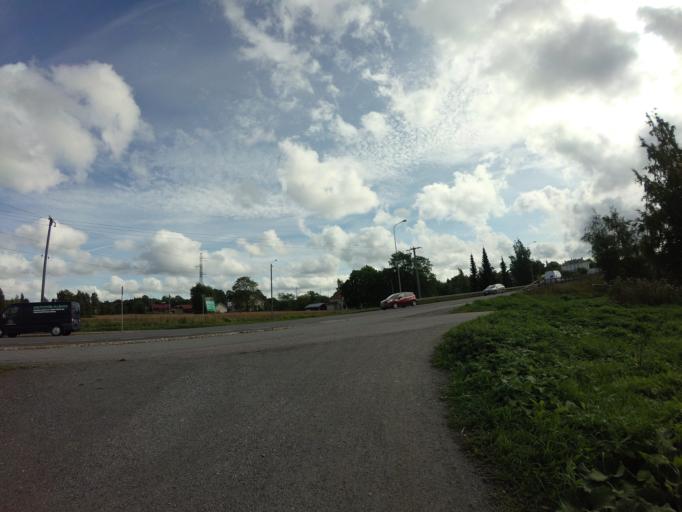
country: FI
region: Varsinais-Suomi
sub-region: Turku
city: Turku
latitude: 60.4661
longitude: 22.3043
